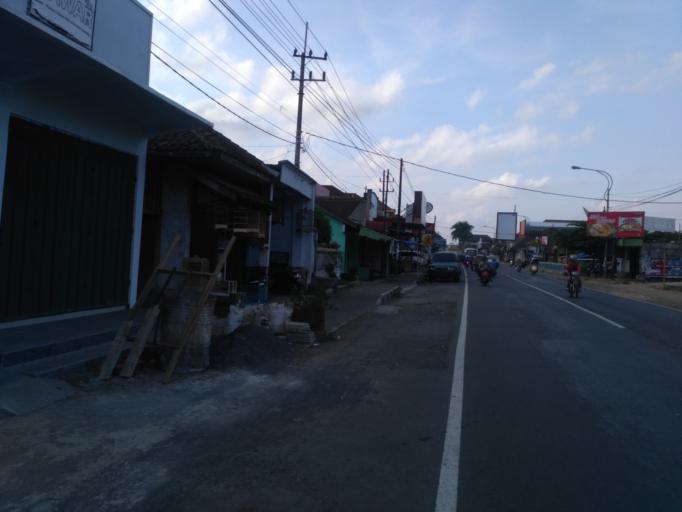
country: ID
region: East Java
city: Bendo
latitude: -8.0707
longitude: 112.5961
